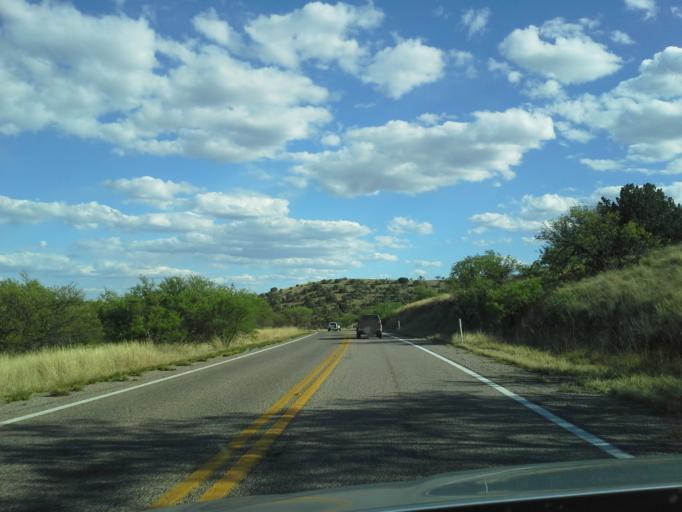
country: US
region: Arizona
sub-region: Pima County
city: Corona de Tucson
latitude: 31.8133
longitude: -110.7120
